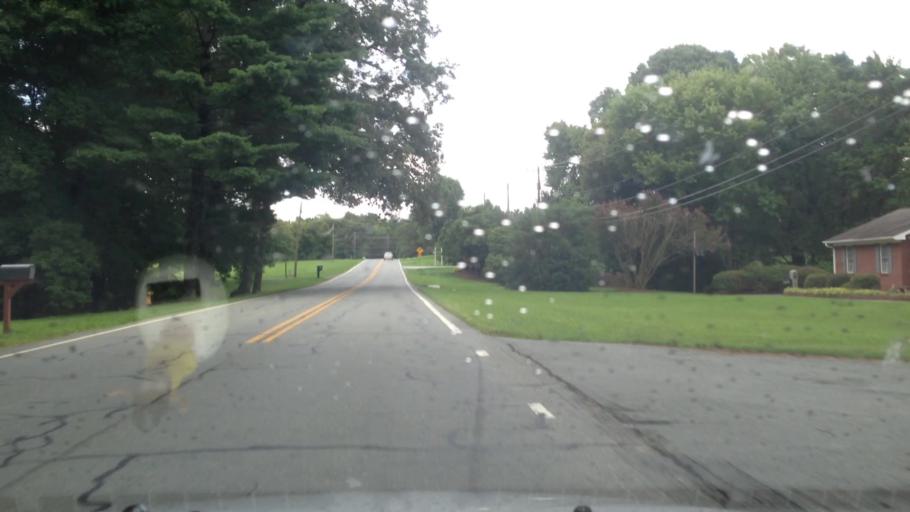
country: US
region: North Carolina
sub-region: Forsyth County
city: Kernersville
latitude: 36.1689
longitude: -80.0561
